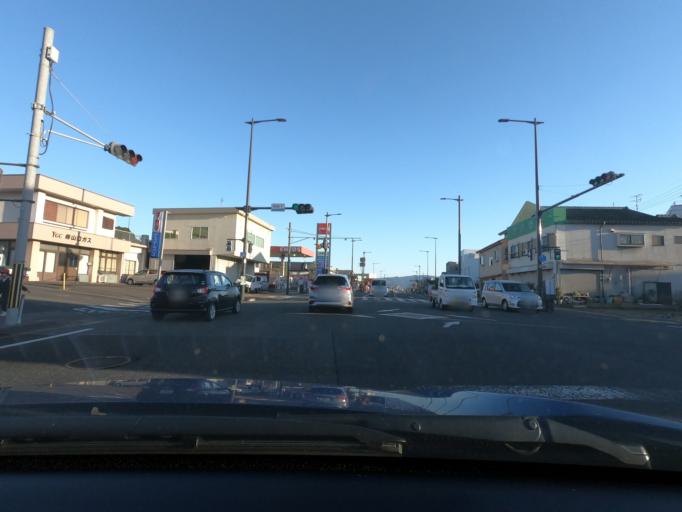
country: JP
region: Kagoshima
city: Satsumasendai
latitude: 31.8315
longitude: 130.2952
